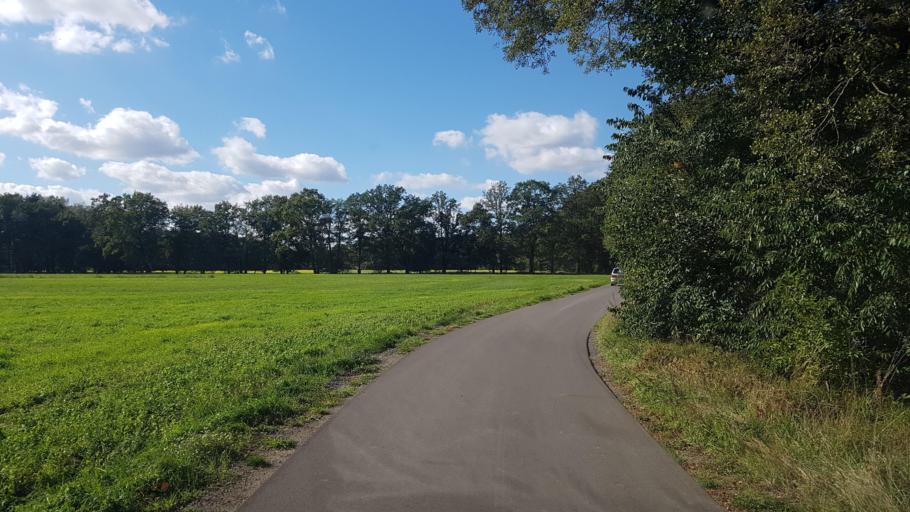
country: DE
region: Brandenburg
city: Drehnow
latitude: 51.8057
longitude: 14.3696
